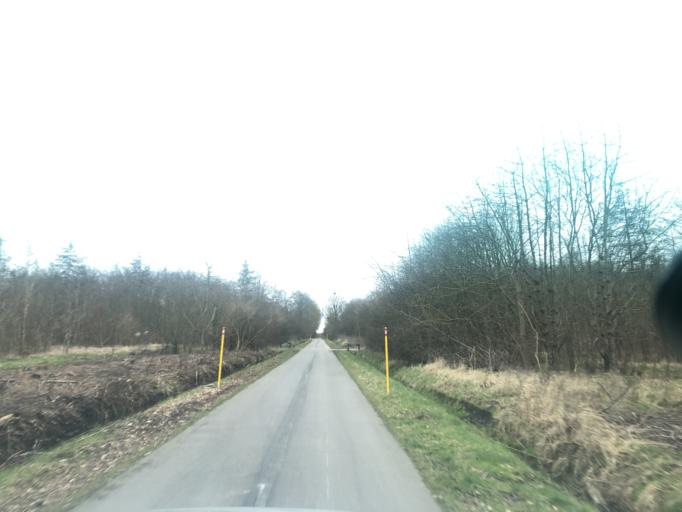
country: DK
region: Capital Region
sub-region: Tarnby Kommune
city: Tarnby
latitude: 55.5699
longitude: 12.5943
